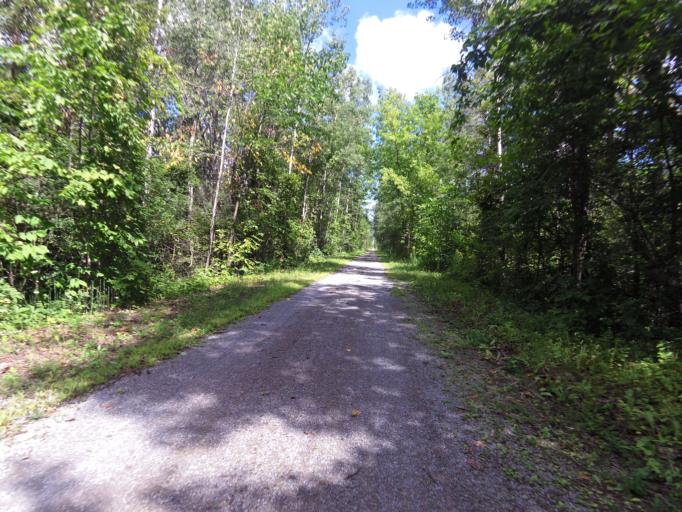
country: CA
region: Ontario
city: Ottawa
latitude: 45.2849
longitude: -75.6261
